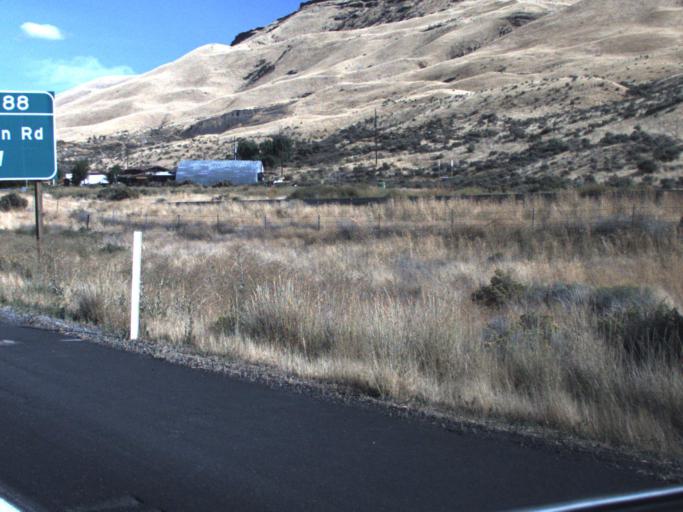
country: US
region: Washington
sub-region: Benton County
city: Prosser
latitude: 46.2421
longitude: -119.6373
